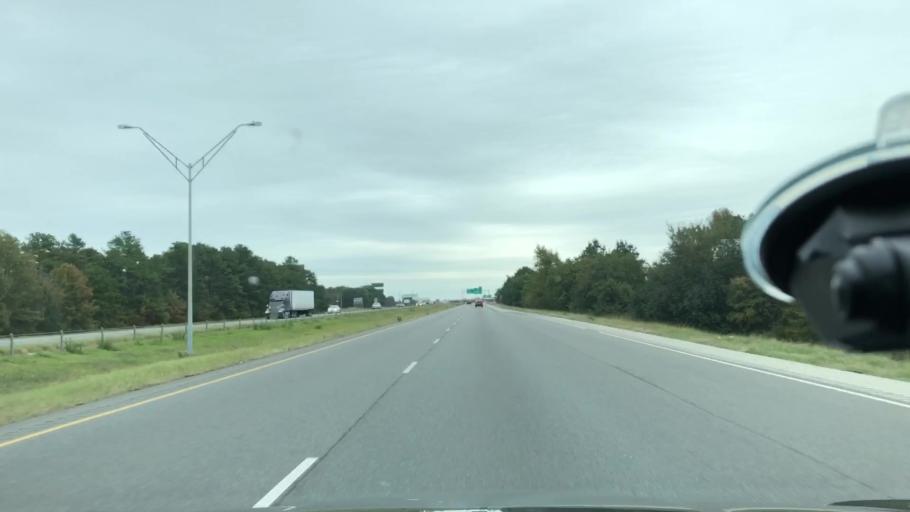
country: US
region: Arkansas
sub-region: Miller County
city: Texarkana
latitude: 33.4767
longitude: -94.0024
